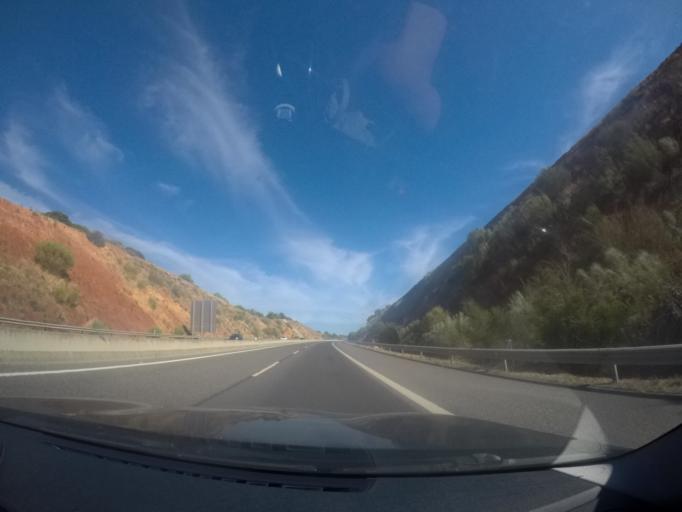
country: PT
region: Faro
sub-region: Portimao
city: Portimao
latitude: 37.1715
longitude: -8.5173
